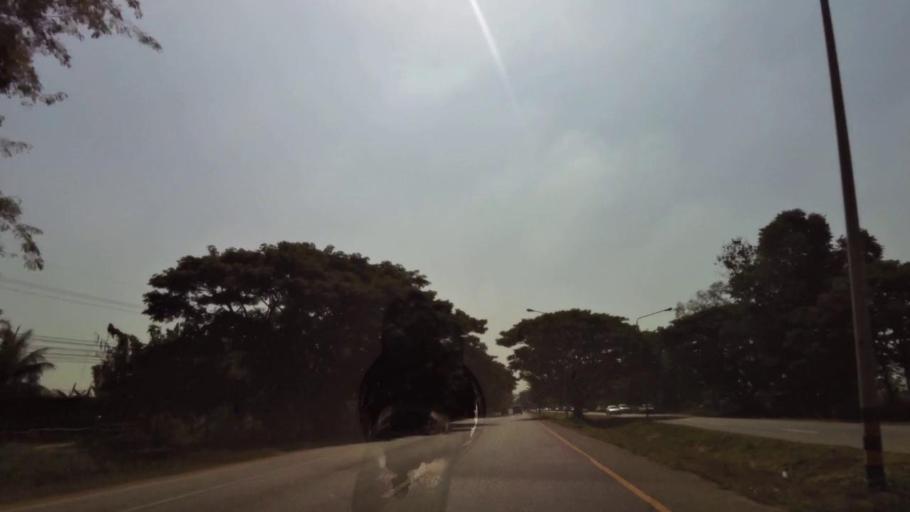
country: TH
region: Phichit
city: Wachira Barami
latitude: 16.3707
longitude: 100.1327
